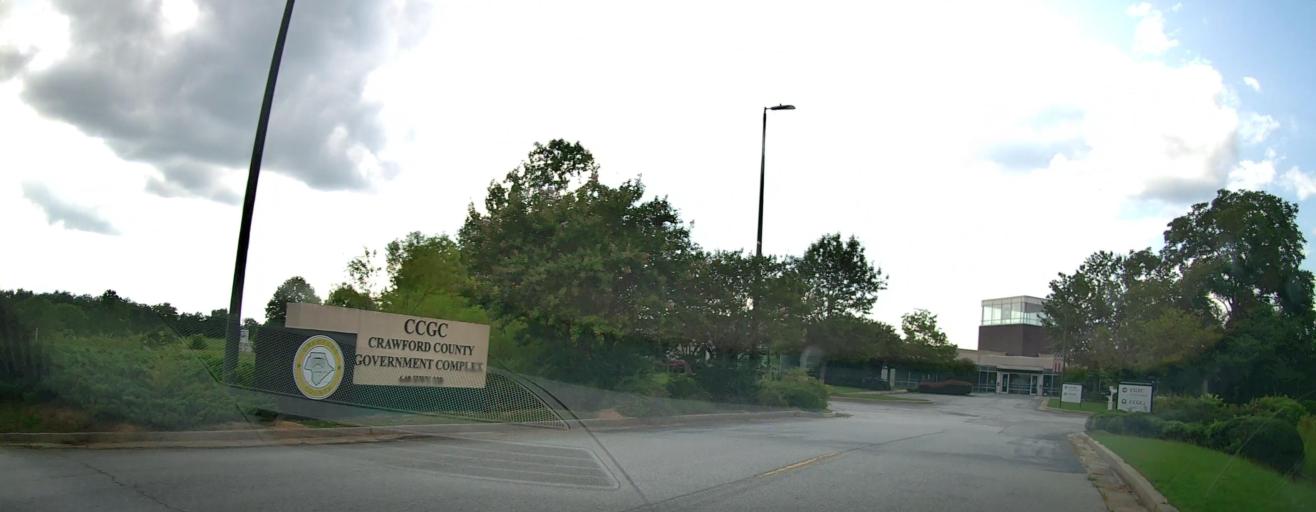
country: US
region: Georgia
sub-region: Crawford County
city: Roberta
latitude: 32.7140
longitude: -84.0204
